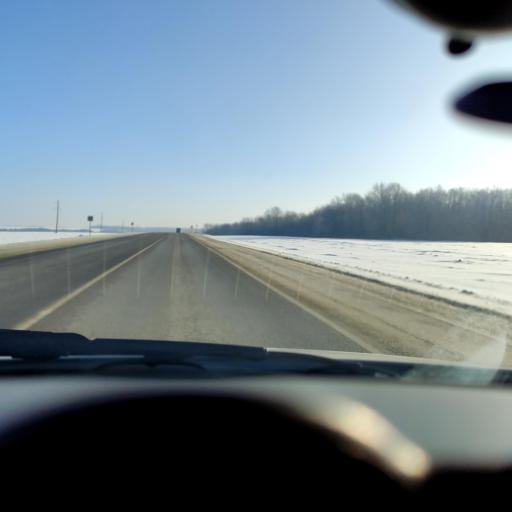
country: RU
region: Kursk
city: Tim
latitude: 51.6518
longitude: 36.9655
